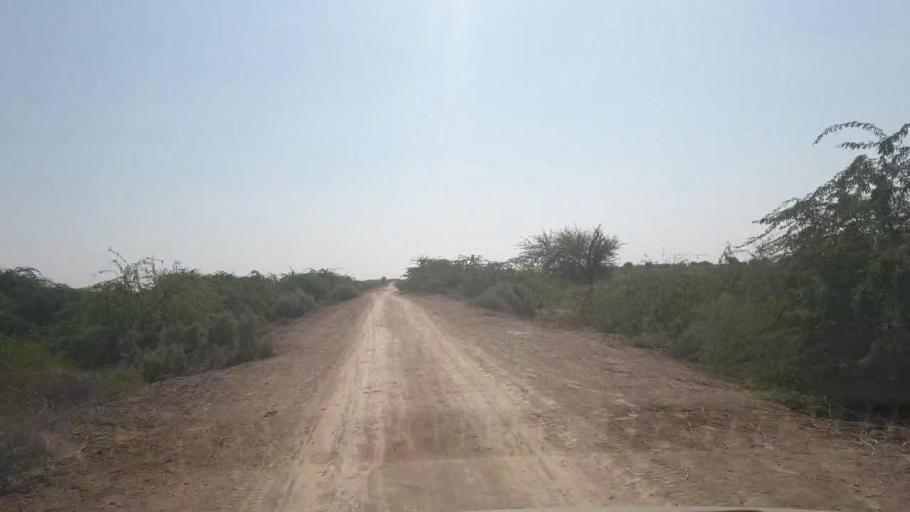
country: PK
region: Sindh
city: Tando Bago
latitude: 24.8832
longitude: 69.1644
